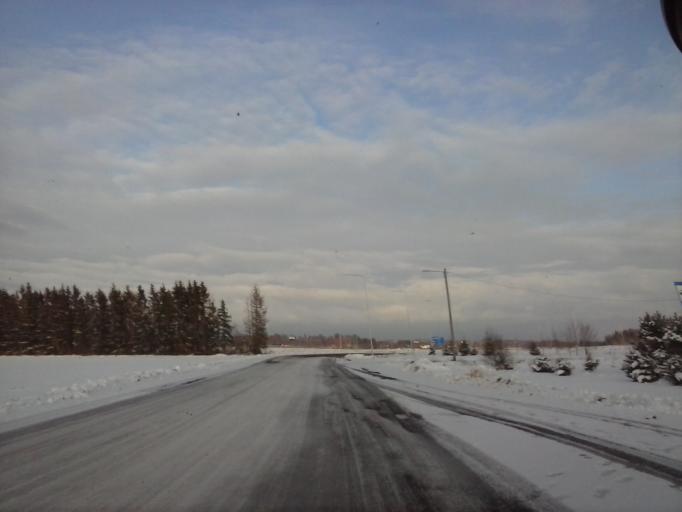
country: EE
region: Tartu
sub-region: Tartu linn
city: Tartu
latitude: 58.3595
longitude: 26.8903
